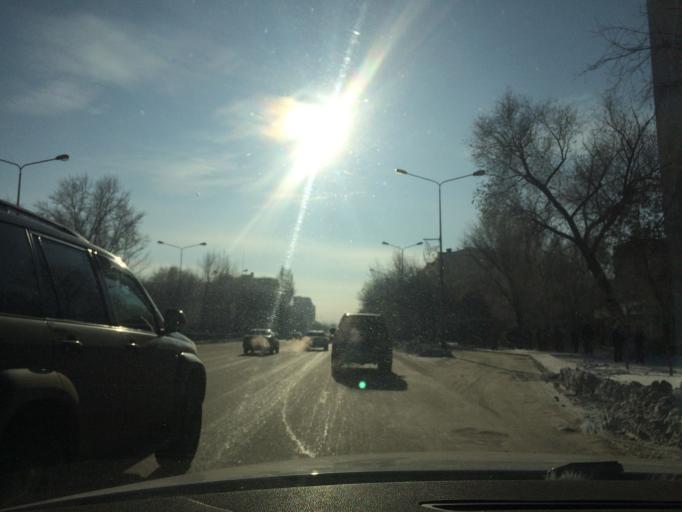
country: KZ
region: Astana Qalasy
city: Astana
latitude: 51.1790
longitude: 71.4101
